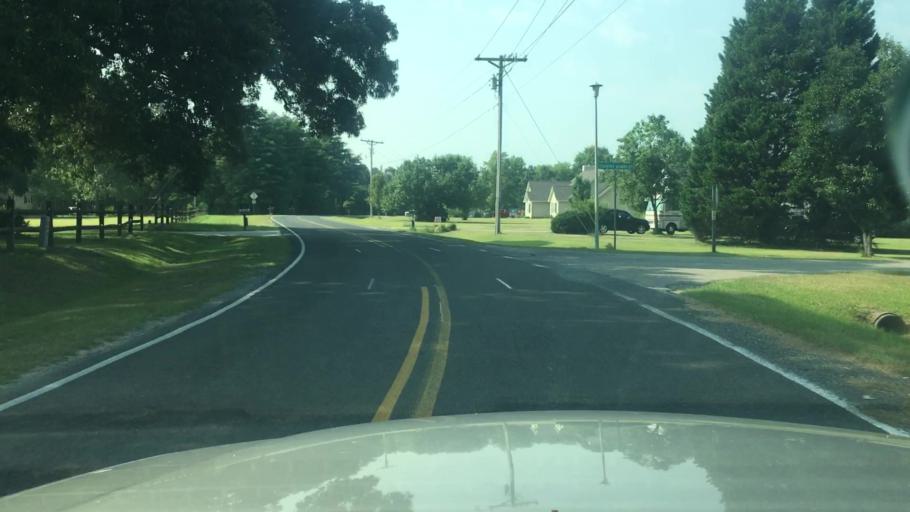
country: US
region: North Carolina
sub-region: Cumberland County
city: Hope Mills
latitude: 34.9070
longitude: -78.8723
